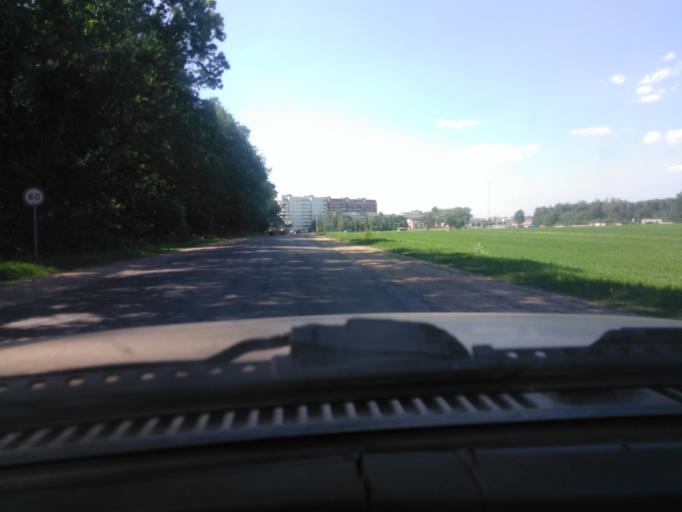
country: BY
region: Mogilev
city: Palykavichy Pyershyya
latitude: 53.9545
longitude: 30.3676
